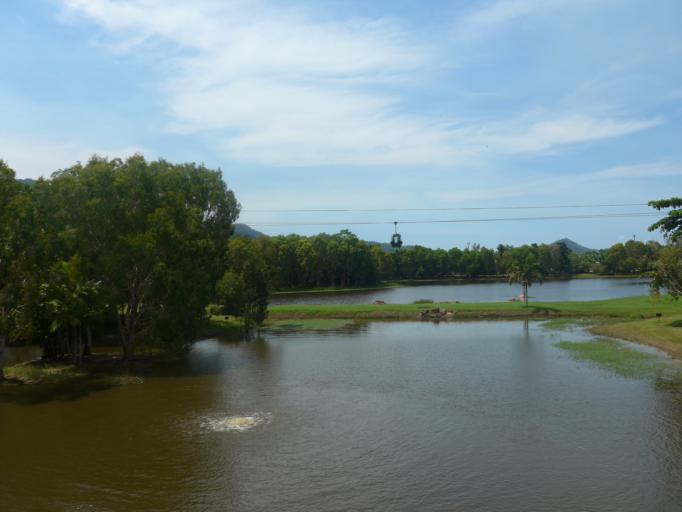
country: AU
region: Queensland
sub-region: Cairns
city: Redlynch
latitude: -16.8486
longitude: 145.6941
